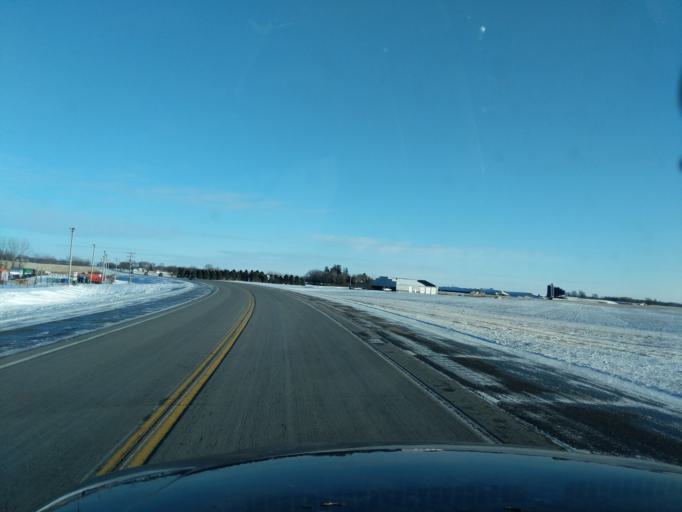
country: US
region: Minnesota
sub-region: McLeod County
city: Hutchinson
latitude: 44.8933
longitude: -94.3184
